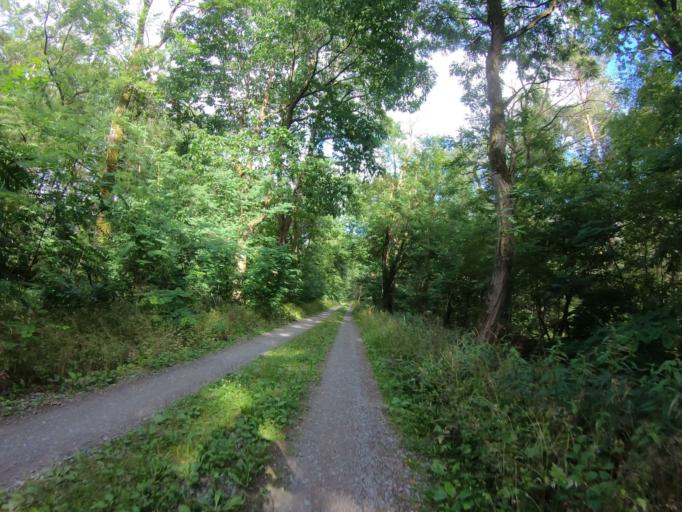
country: DE
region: Lower Saxony
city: Calberlah
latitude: 52.4613
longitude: 10.6337
